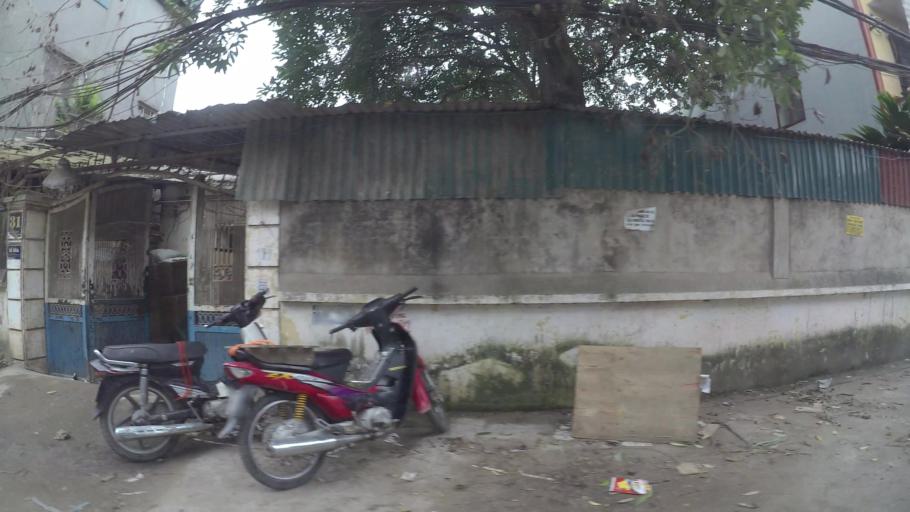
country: VN
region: Ha Noi
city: Tay Ho
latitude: 21.0681
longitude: 105.8303
